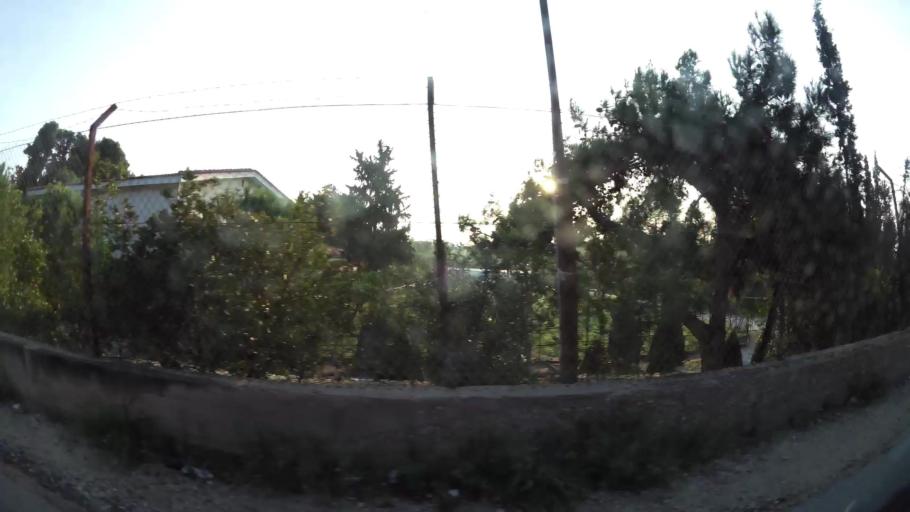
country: GR
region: Attica
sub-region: Nomarchia Athinas
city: Kamateron
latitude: 38.0499
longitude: 23.7193
